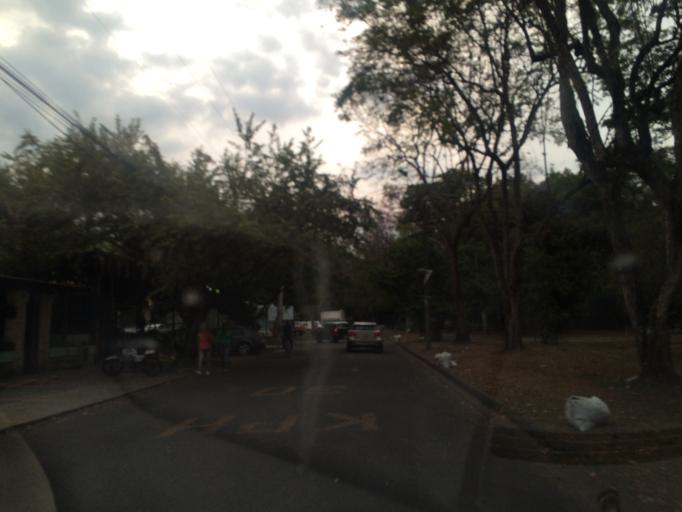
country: CO
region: Valle del Cauca
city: Cali
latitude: 3.3652
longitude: -76.5317
